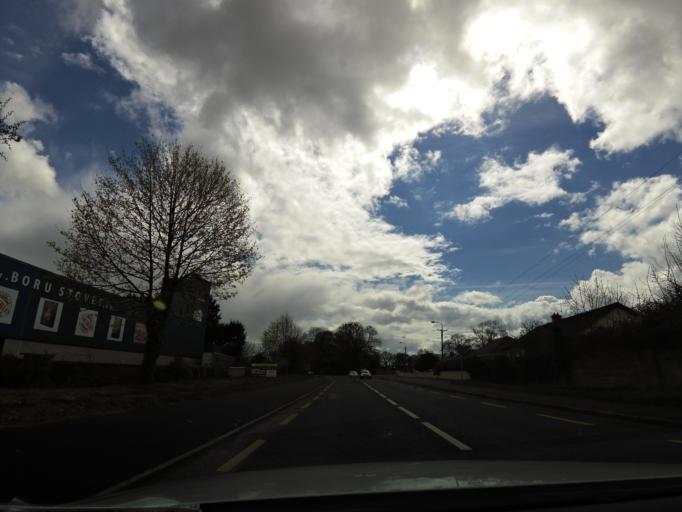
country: IE
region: Munster
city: Thurles
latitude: 52.6873
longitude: -7.8130
